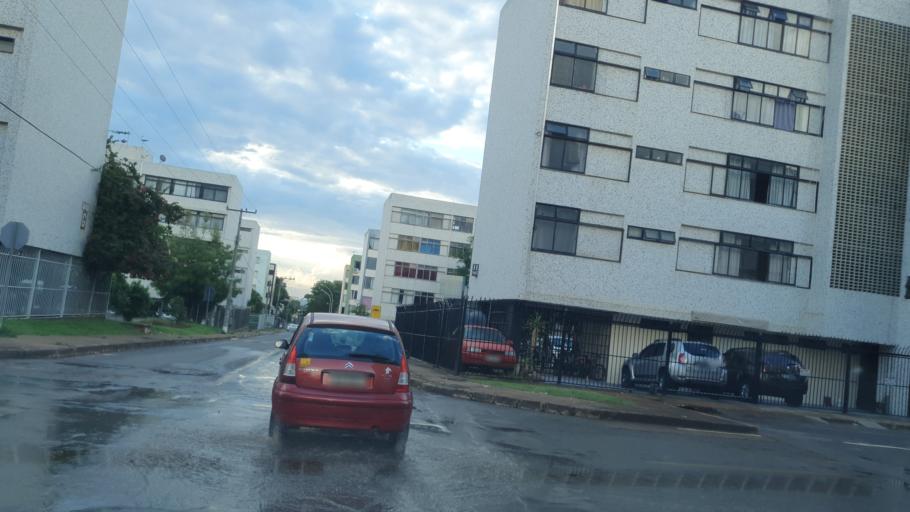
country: BR
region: Federal District
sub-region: Brasilia
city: Brasilia
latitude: -15.7988
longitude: -47.9384
